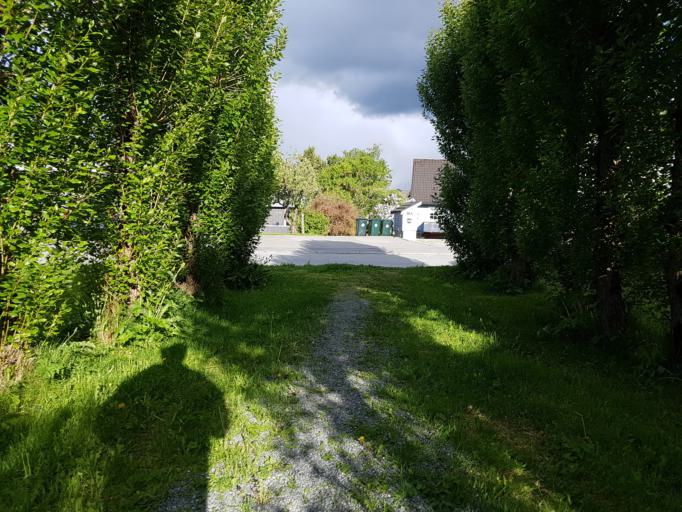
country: NO
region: Sor-Trondelag
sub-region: Trondheim
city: Trondheim
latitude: 63.4313
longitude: 10.4624
